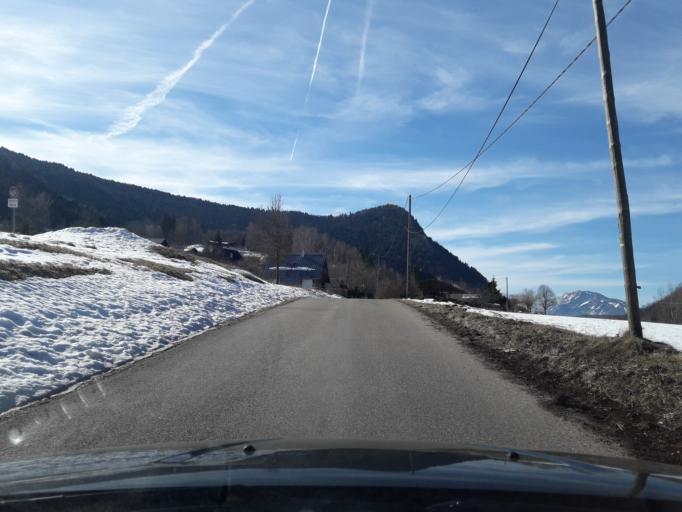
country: FR
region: Rhone-Alpes
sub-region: Departement de l'Isere
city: Le Sappey-en-Chartreuse
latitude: 45.2521
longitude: 5.7702
